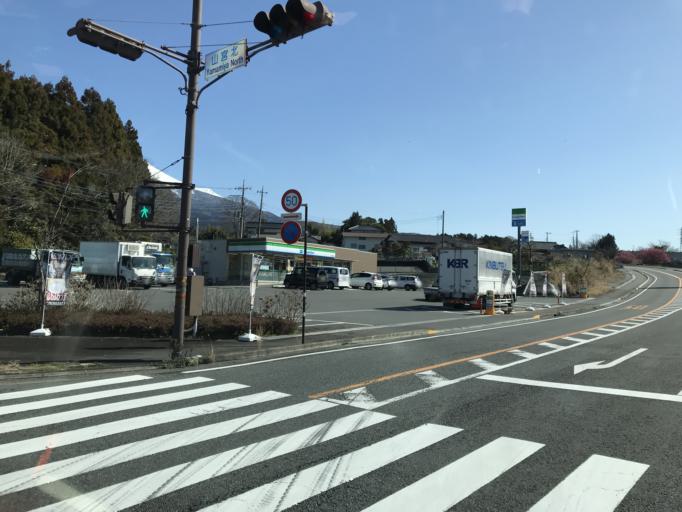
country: JP
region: Shizuoka
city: Fujinomiya
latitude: 35.2645
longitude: 138.6340
